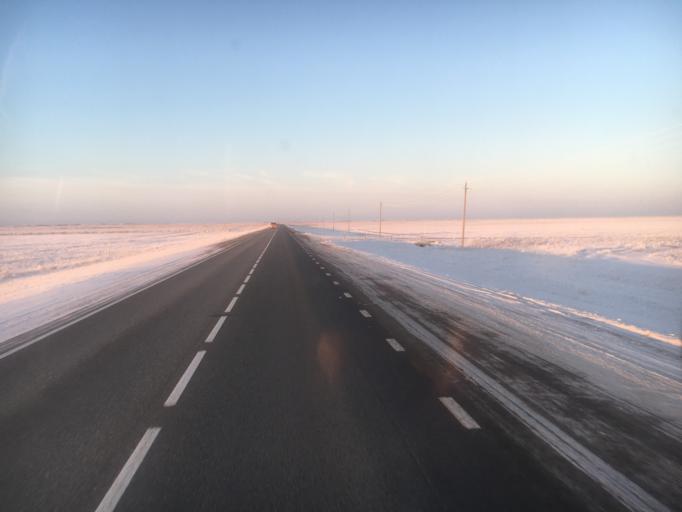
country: KZ
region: Soltustik Qazaqstan
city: Smirnovo
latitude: 54.2736
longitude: 69.1590
